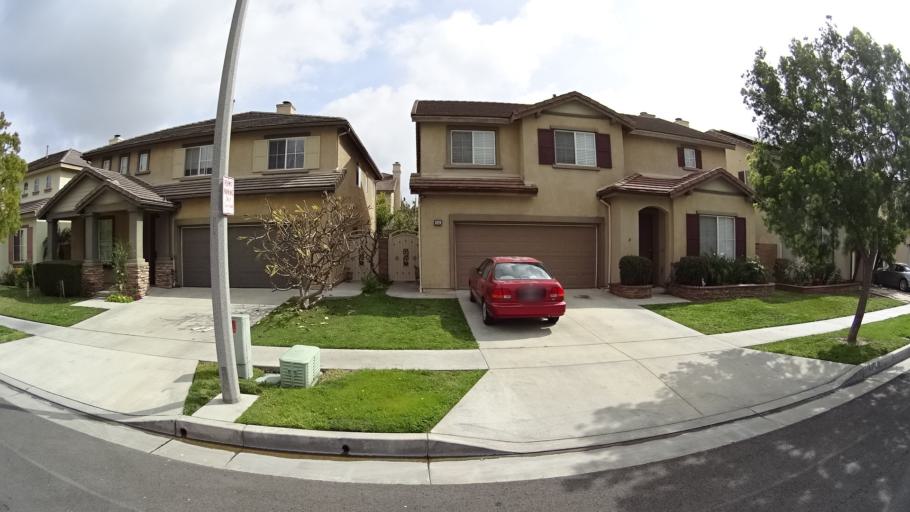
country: US
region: California
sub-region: Orange County
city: Stanton
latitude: 33.8238
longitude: -117.9967
